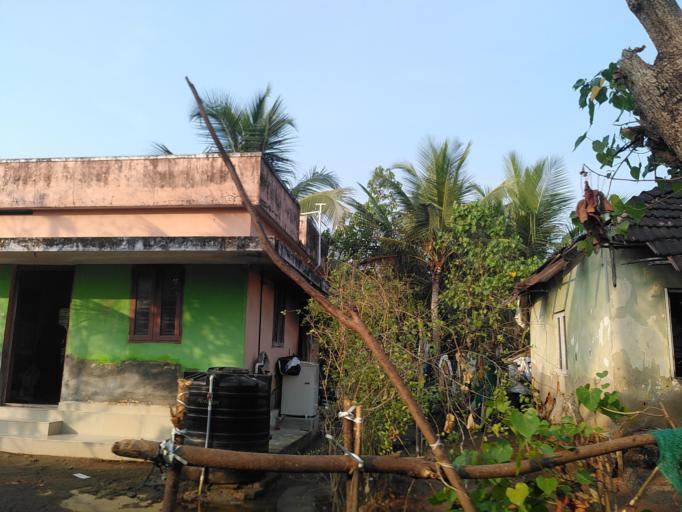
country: IN
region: Kerala
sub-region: Alappuzha
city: Arukutti
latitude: 9.9225
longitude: 76.3298
